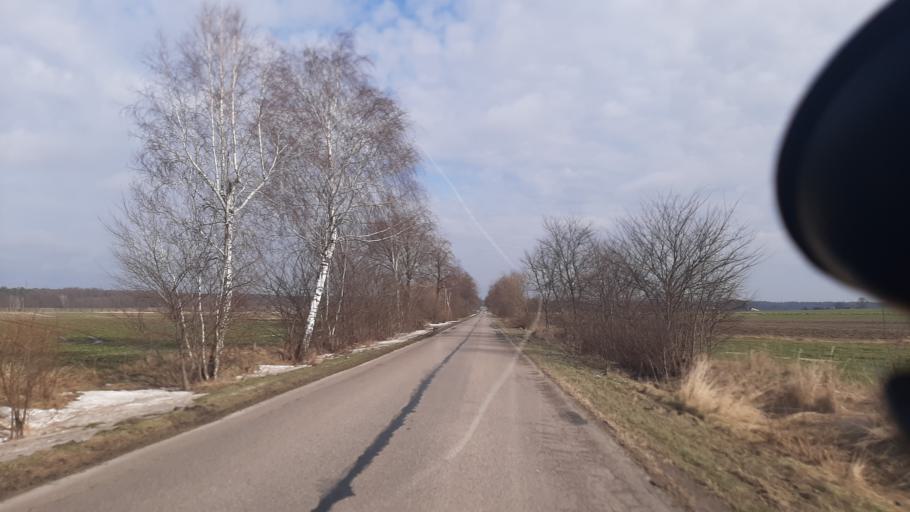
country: PL
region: Lublin Voivodeship
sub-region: Powiat lubartowski
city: Wola Sernicka
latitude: 51.4618
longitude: 22.7089
